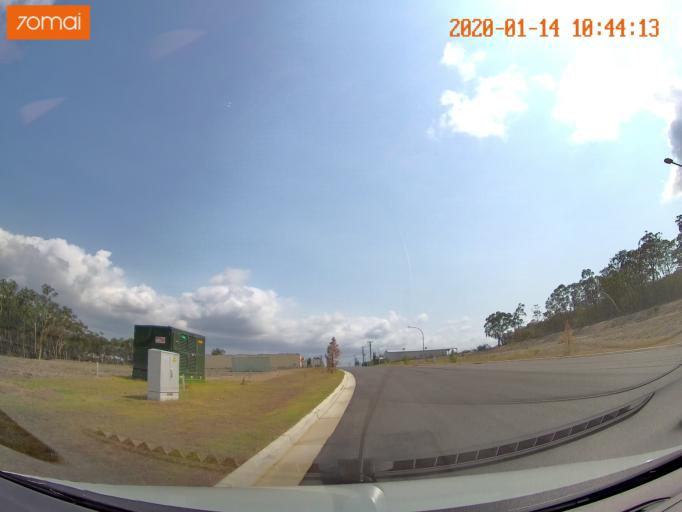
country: AU
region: New South Wales
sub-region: Lake Macquarie Shire
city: Dora Creek
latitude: -33.1224
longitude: 151.4725
